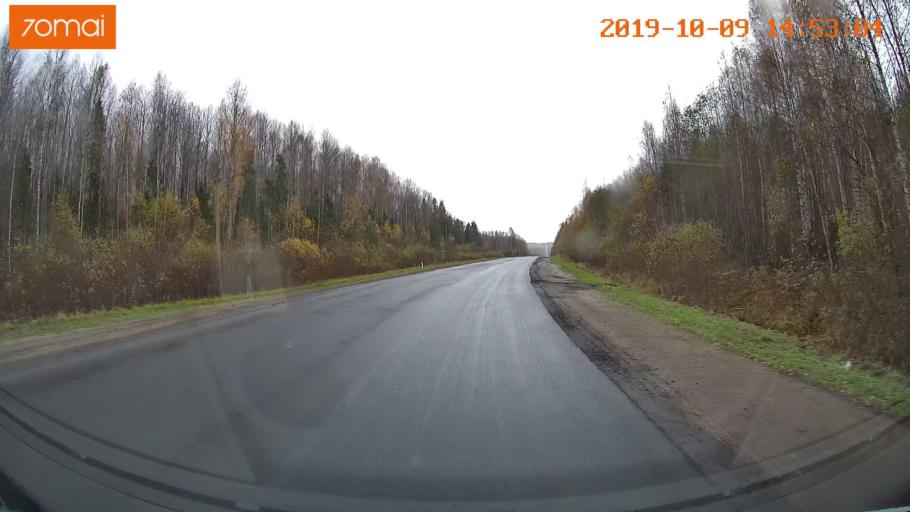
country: RU
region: Kostroma
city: Chistyye Bory
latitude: 58.3723
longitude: 41.6363
